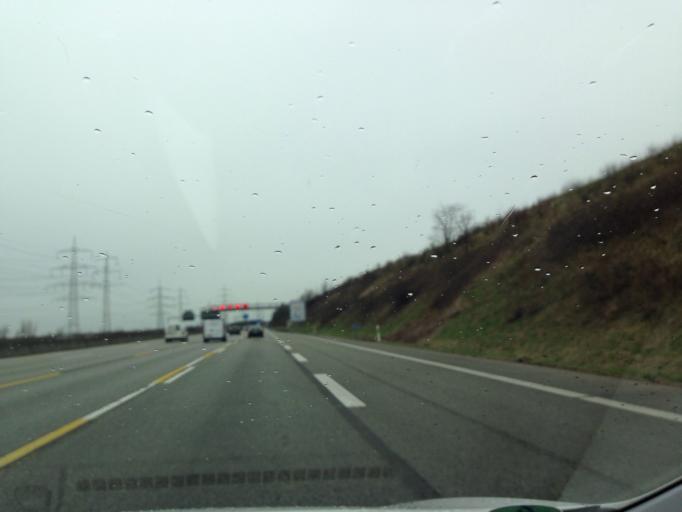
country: DE
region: North Rhine-Westphalia
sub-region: Regierungsbezirk Dusseldorf
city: Neuss
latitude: 51.1858
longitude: 6.6639
